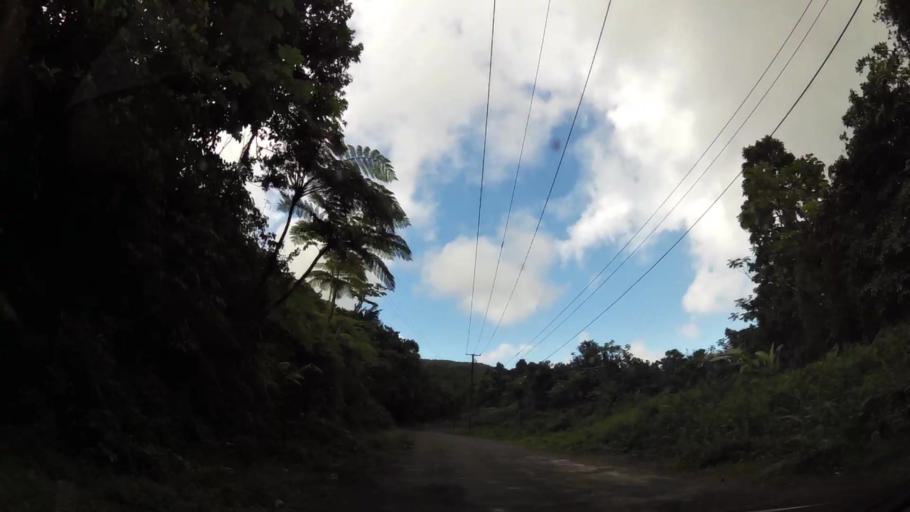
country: DM
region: Saint Paul
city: Pont Casse
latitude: 15.3905
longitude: -61.3127
